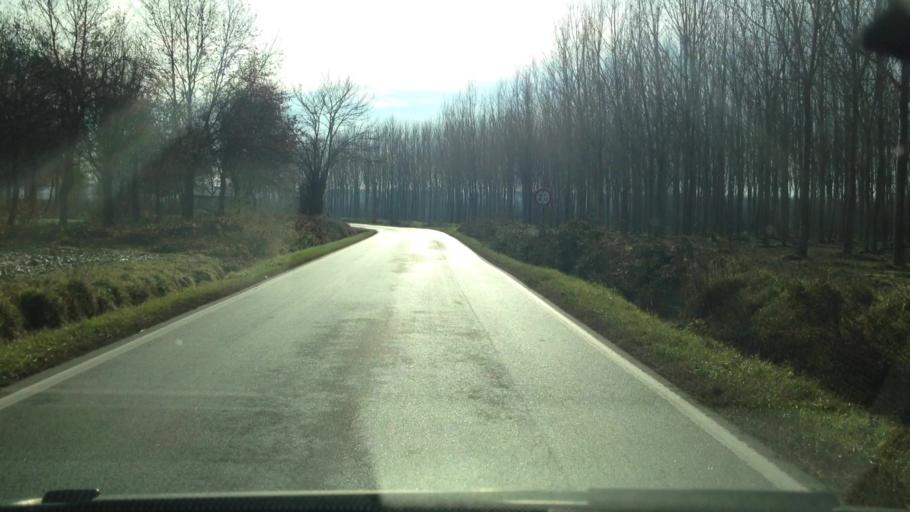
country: IT
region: Piedmont
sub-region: Provincia di Alessandria
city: Quattordio
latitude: 44.8873
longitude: 8.4044
